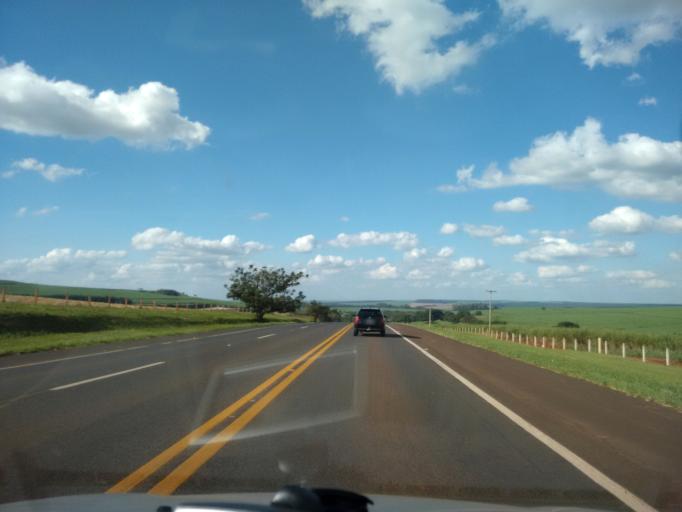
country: BR
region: Sao Paulo
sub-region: Americo Brasiliense
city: Americo Brasiliense
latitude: -21.7636
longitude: -48.0813
